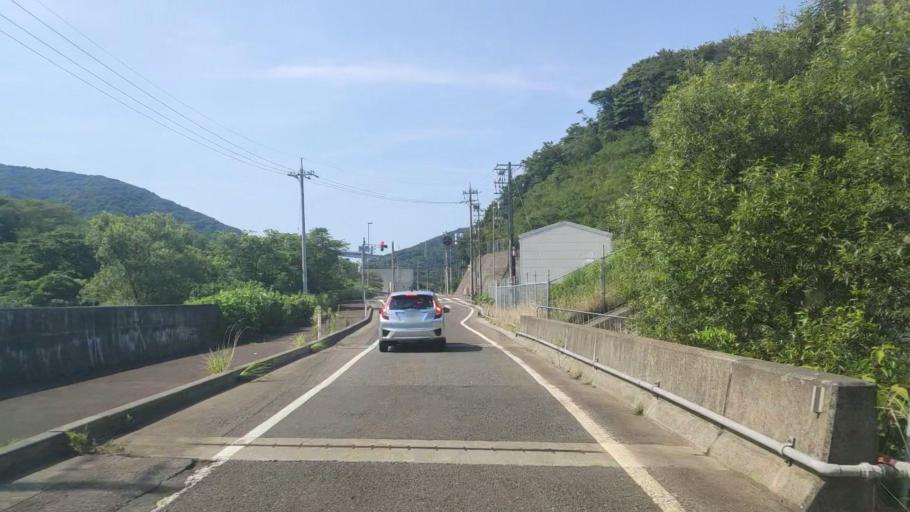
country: JP
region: Fukui
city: Tsuruga
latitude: 35.6146
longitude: 136.0837
